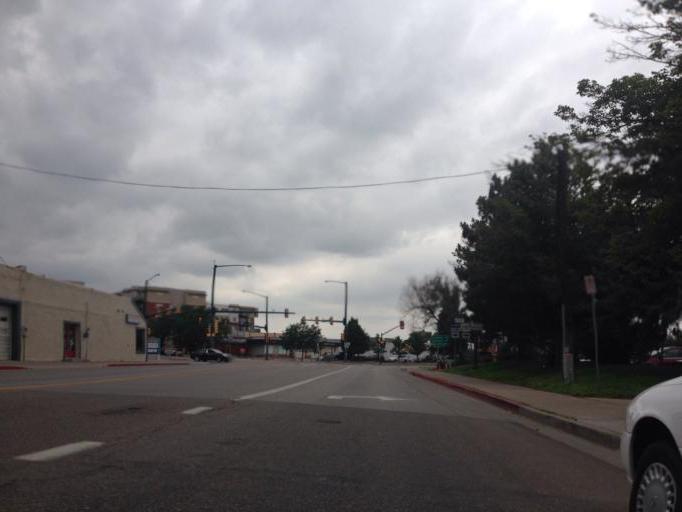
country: US
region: Colorado
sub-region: Larimer County
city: Fort Collins
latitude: 40.5903
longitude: -105.0760
